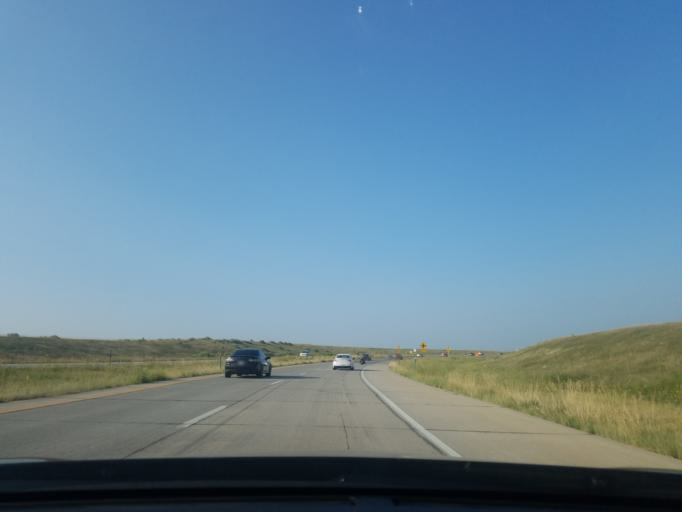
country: US
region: Colorado
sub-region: Larimer County
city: Campion
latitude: 40.3325
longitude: -105.1003
